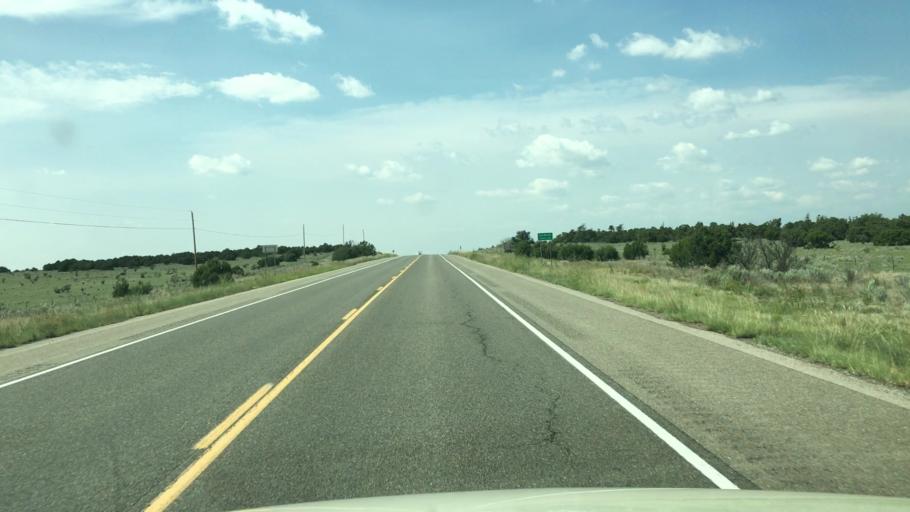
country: US
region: New Mexico
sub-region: Torrance County
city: Moriarty
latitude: 35.0416
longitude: -105.6828
